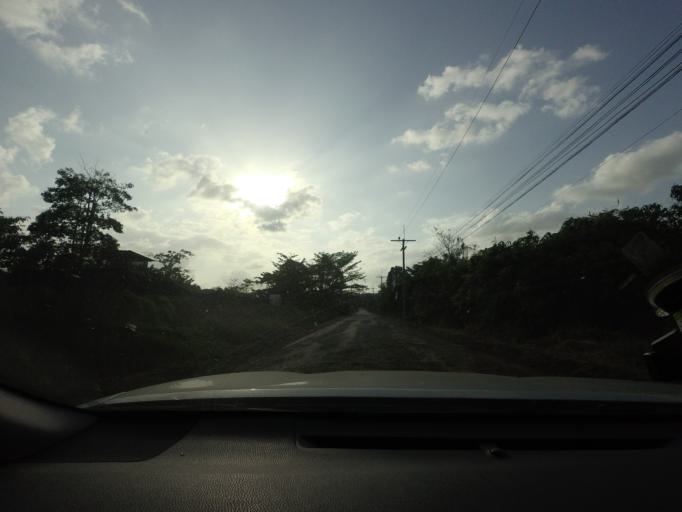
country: TH
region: Pattani
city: Mae Lan
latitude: 6.6157
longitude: 101.2405
